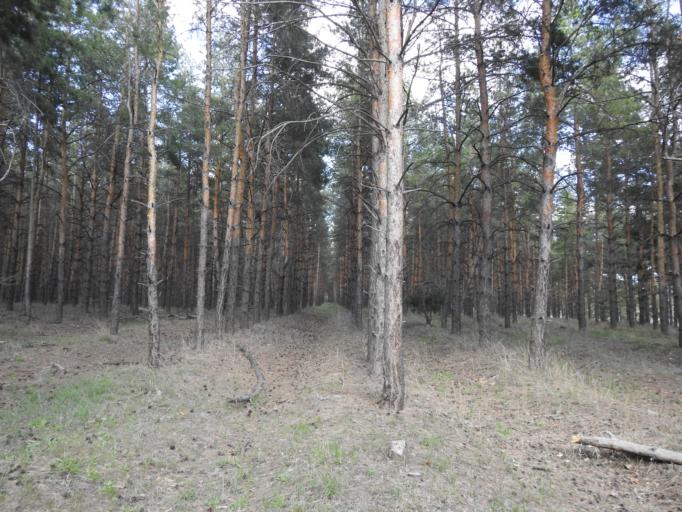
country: RU
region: Saratov
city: Krasnyy Yar
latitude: 51.5852
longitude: 46.5511
